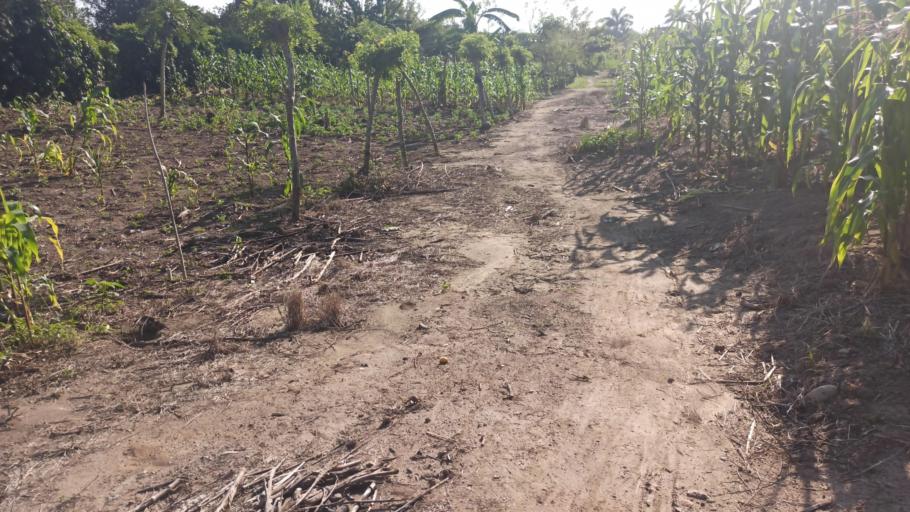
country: MX
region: Veracruz
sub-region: Martinez de la Torre
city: El Progreso
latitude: 20.0879
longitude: -97.0187
